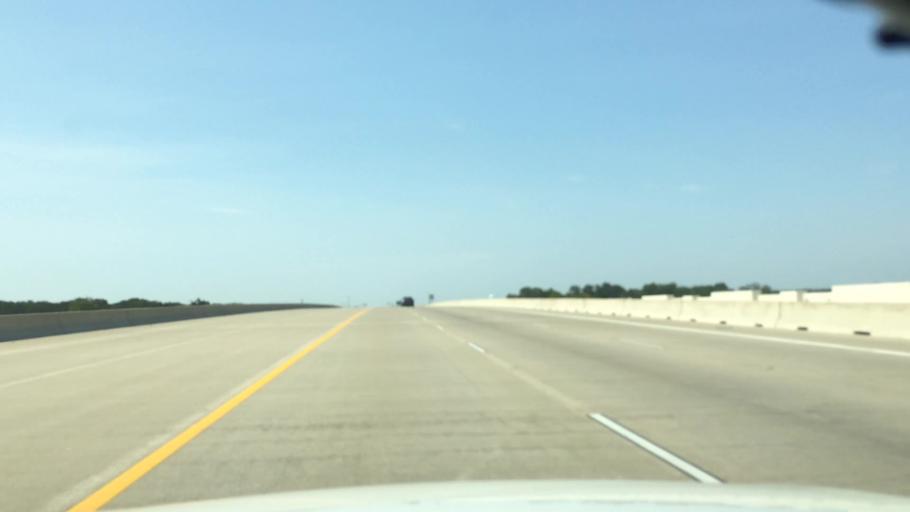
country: US
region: Texas
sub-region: Dallas County
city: Grand Prairie
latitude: 32.7997
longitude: -97.0184
